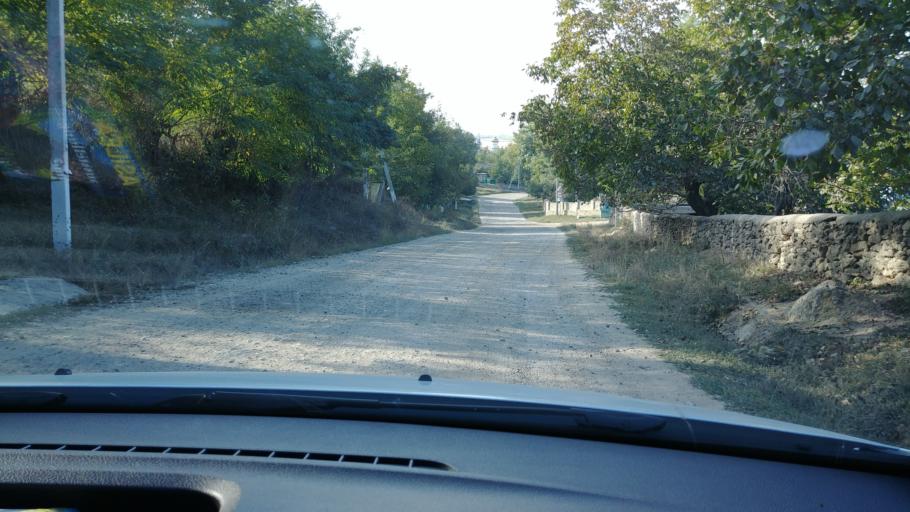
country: MD
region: Rezina
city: Rezina
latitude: 47.7465
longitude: 28.8869
